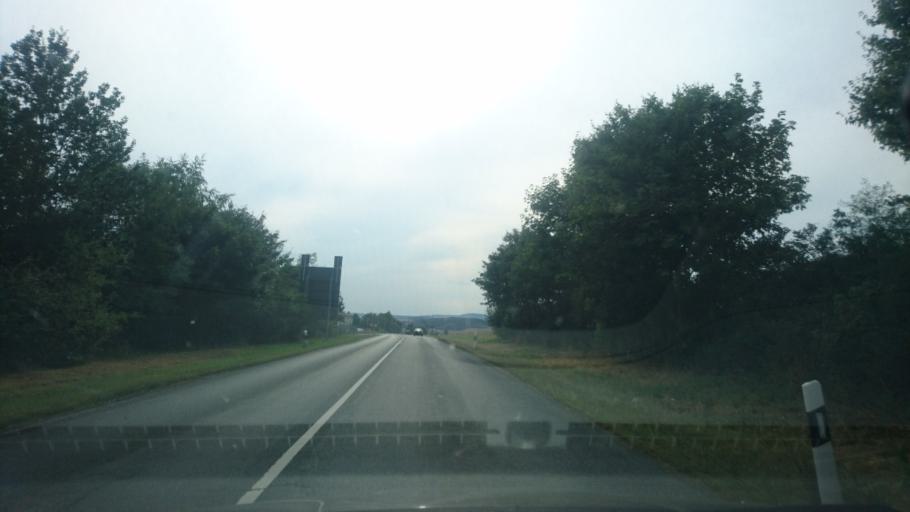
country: DE
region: Bavaria
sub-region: Upper Franconia
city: Leupoldsgrun
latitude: 50.2910
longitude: 11.8071
